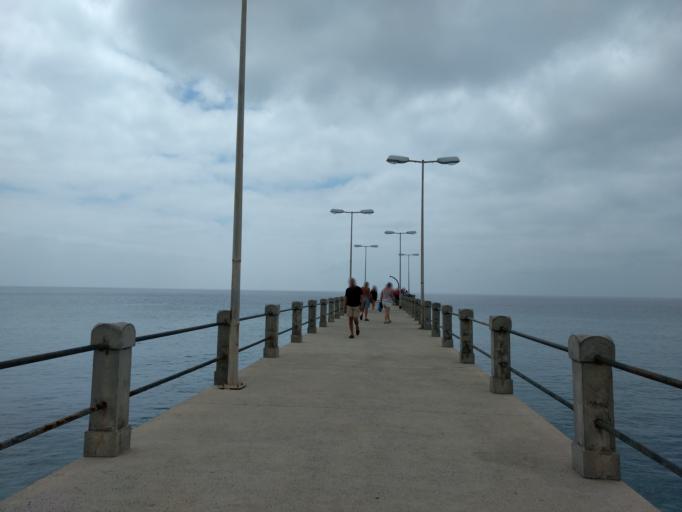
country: PT
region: Madeira
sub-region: Porto Santo
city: Vila de Porto Santo
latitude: 33.0570
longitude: -16.3343
